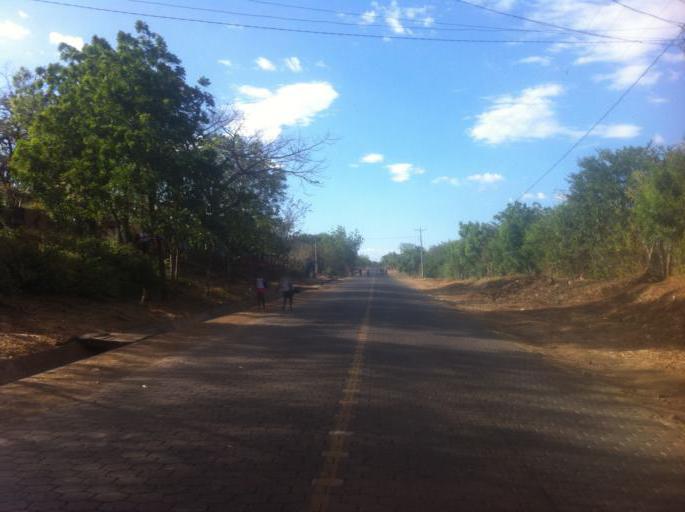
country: NI
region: Managua
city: Masachapa
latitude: 11.8169
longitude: -86.4968
